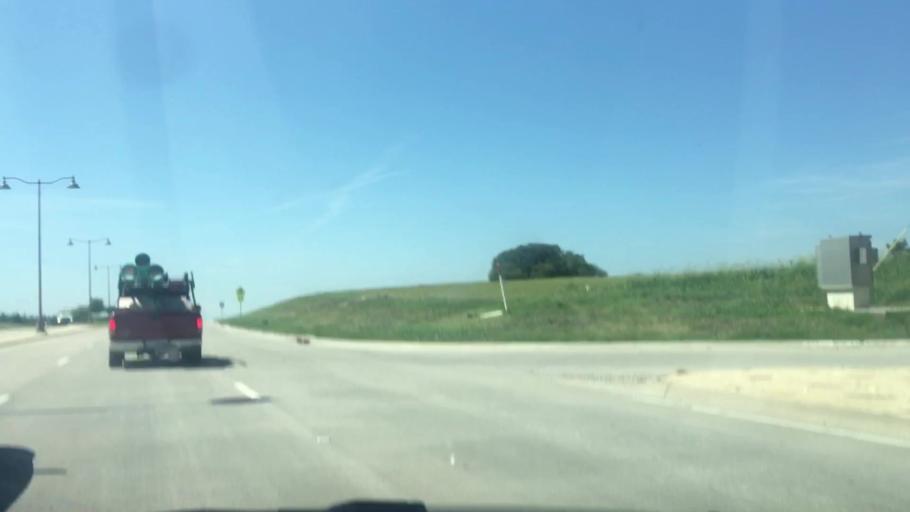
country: US
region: Texas
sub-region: Collin County
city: Prosper
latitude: 33.2323
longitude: -96.7898
